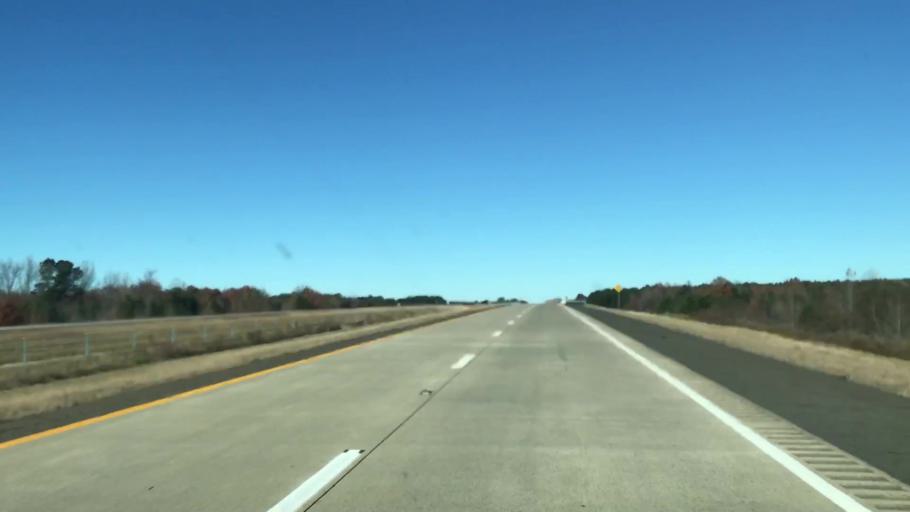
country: US
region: Texas
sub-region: Bowie County
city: Texarkana
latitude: 33.2487
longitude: -93.8840
